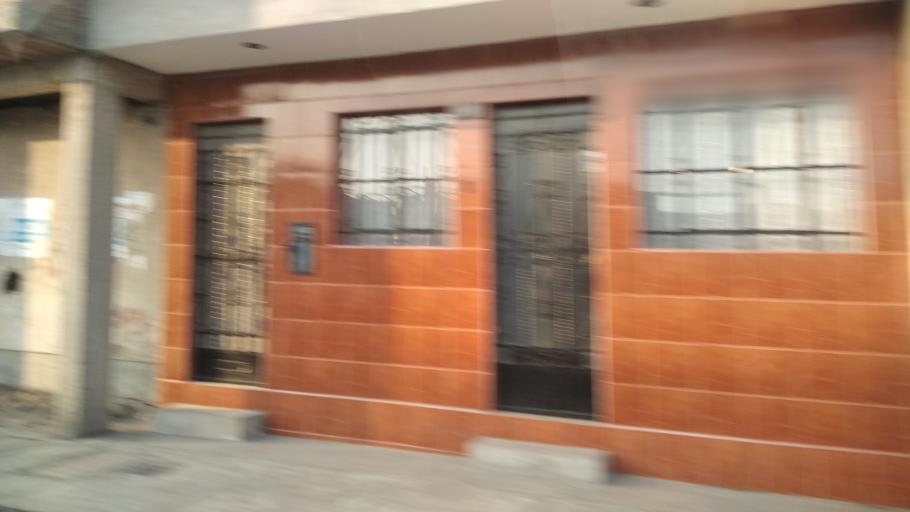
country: PE
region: Lima
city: Lima
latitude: -12.0194
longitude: -76.9866
